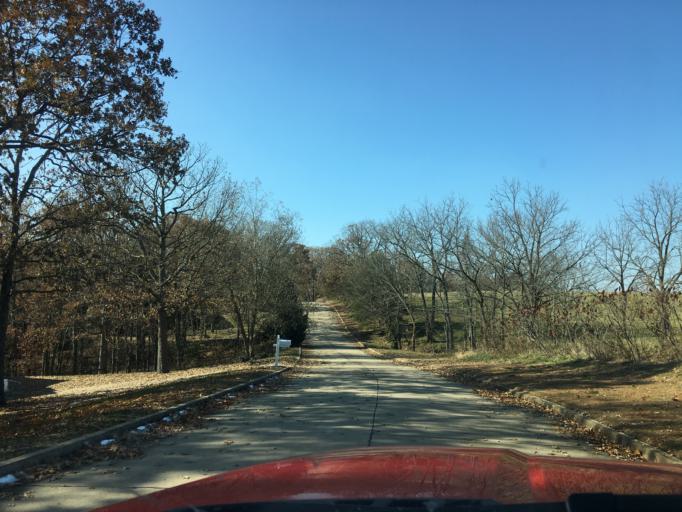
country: US
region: Missouri
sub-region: Cole County
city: Wardsville
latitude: 38.4840
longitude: -92.1798
